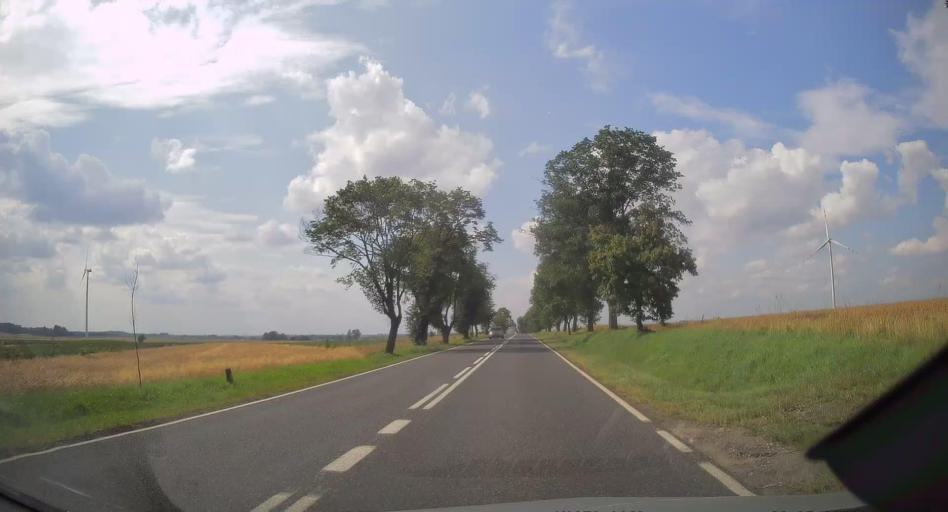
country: PL
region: Lodz Voivodeship
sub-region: Powiat skierniewicki
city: Gluchow
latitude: 51.7892
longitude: 20.0460
